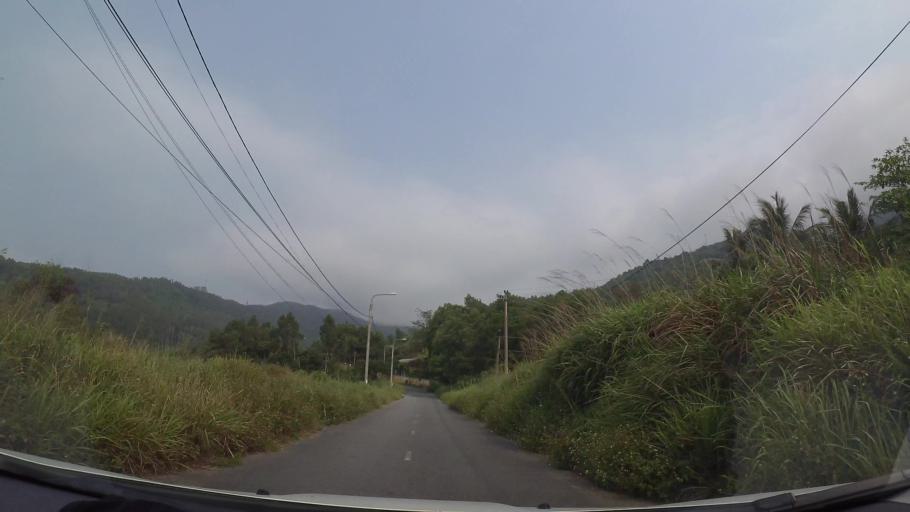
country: VN
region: Da Nang
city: Son Tra
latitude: 16.1084
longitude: 108.2614
